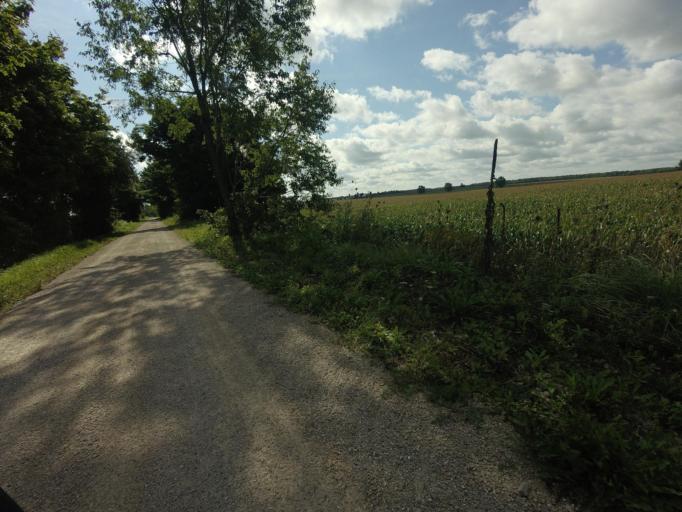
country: CA
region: Ontario
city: Huron East
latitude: 43.7117
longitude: -81.3760
